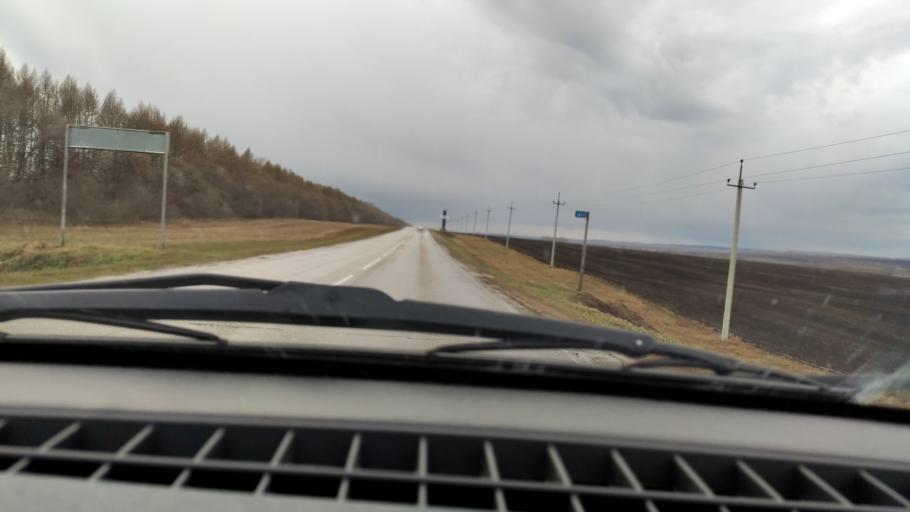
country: RU
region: Bashkortostan
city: Chekmagush
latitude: 55.1099
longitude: 54.9377
